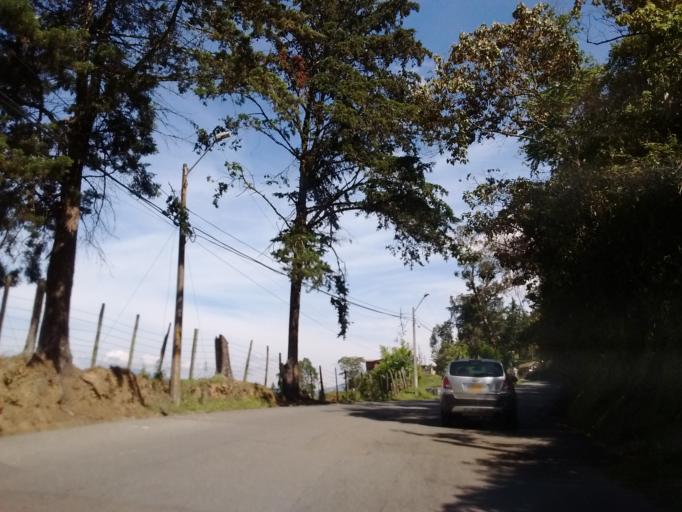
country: CO
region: Antioquia
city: Medellin
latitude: 6.2313
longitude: -75.5165
